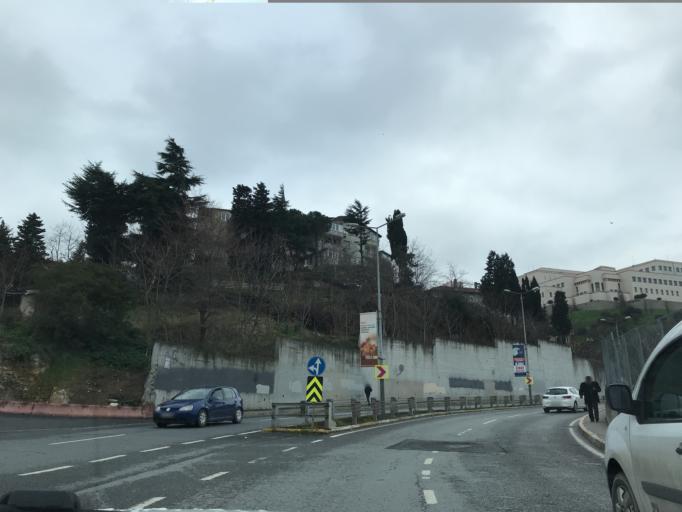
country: TR
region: Istanbul
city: Sisli
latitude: 41.1169
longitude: 29.0495
